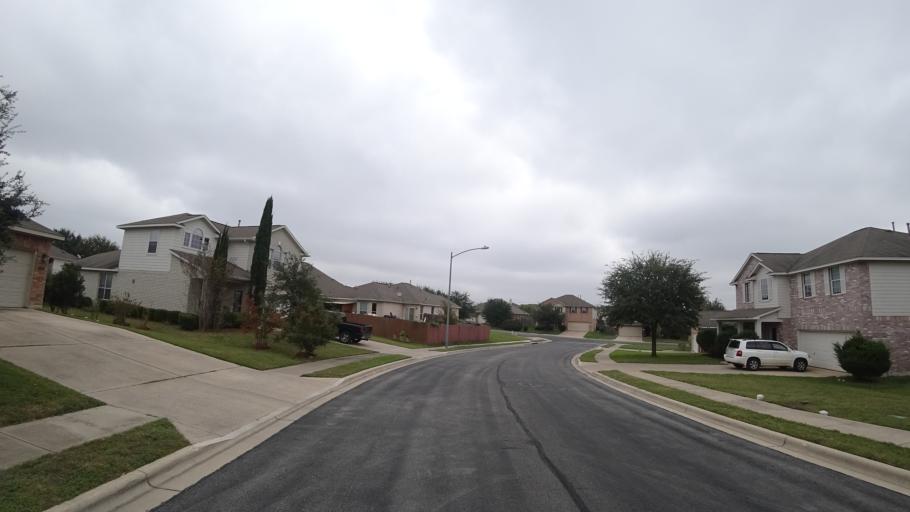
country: US
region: Texas
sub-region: Travis County
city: Pflugerville
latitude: 30.3726
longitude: -97.6514
